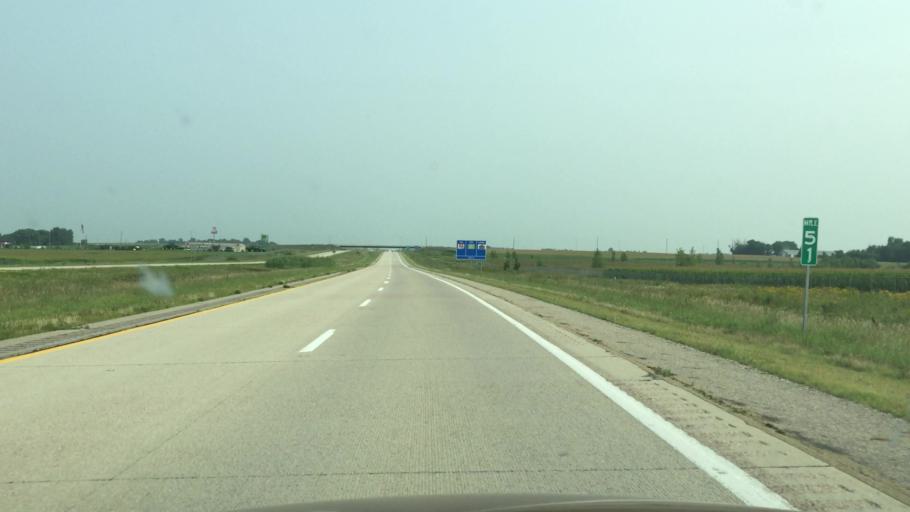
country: US
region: Iowa
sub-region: Osceola County
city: Sibley
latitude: 43.3955
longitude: -95.7171
